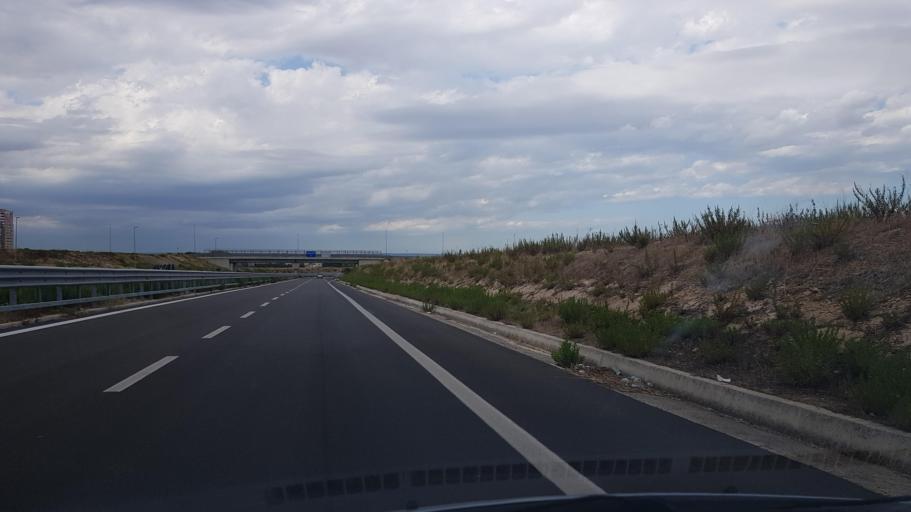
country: IT
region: Apulia
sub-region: Provincia di Taranto
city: Taranto
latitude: 40.4526
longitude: 17.2848
